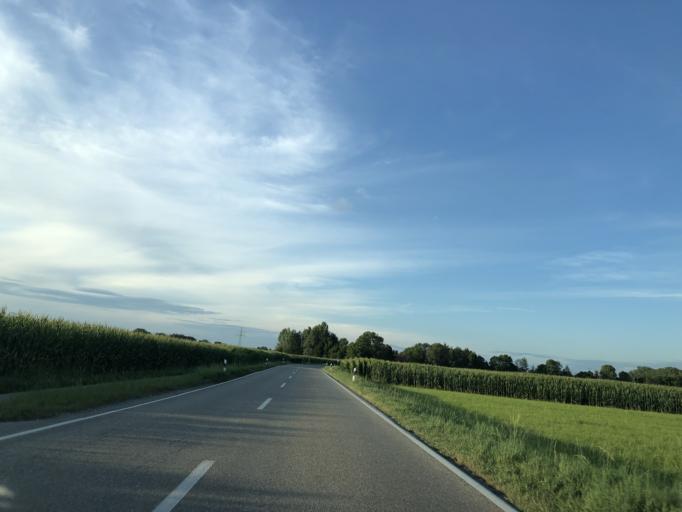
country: DE
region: Bavaria
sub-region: Upper Bavaria
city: Finsing
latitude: 48.2337
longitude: 11.8155
